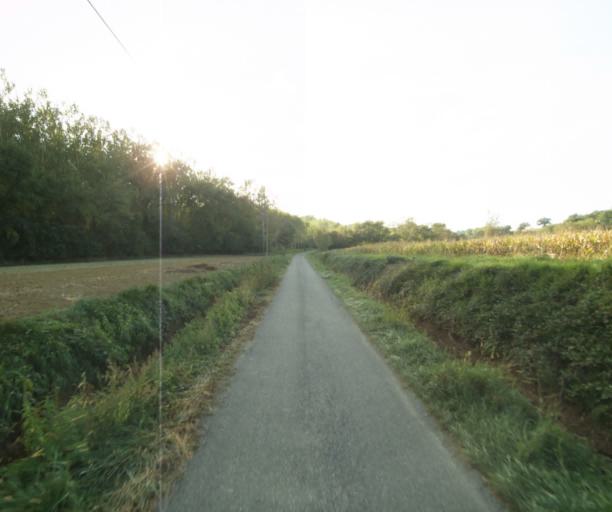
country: FR
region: Midi-Pyrenees
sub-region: Departement du Gers
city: Gondrin
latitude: 43.8828
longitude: 0.2763
